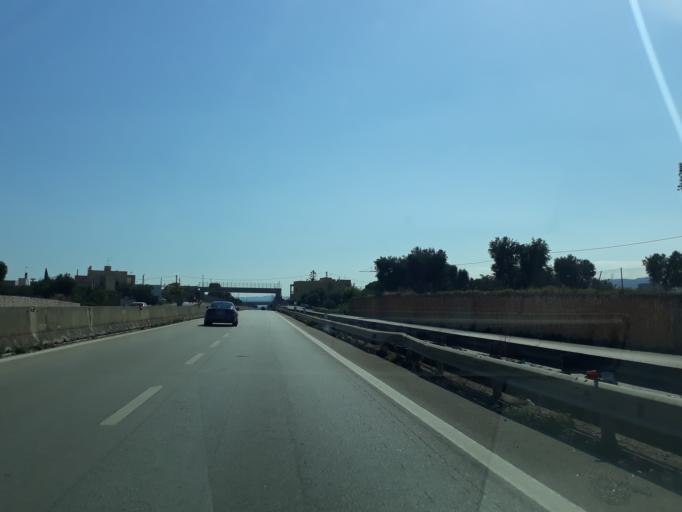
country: IT
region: Apulia
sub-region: Provincia di Brindisi
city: Fasano
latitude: 40.8864
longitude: 17.3350
